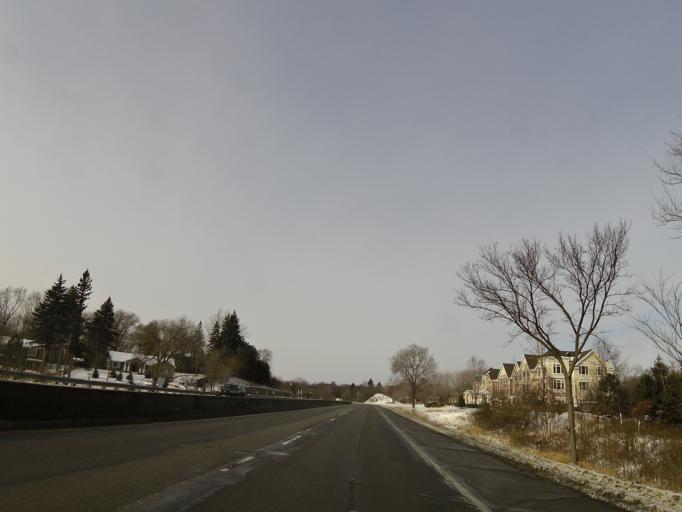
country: US
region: Minnesota
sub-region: Hennepin County
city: Minnetonka
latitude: 44.9109
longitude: -93.5148
